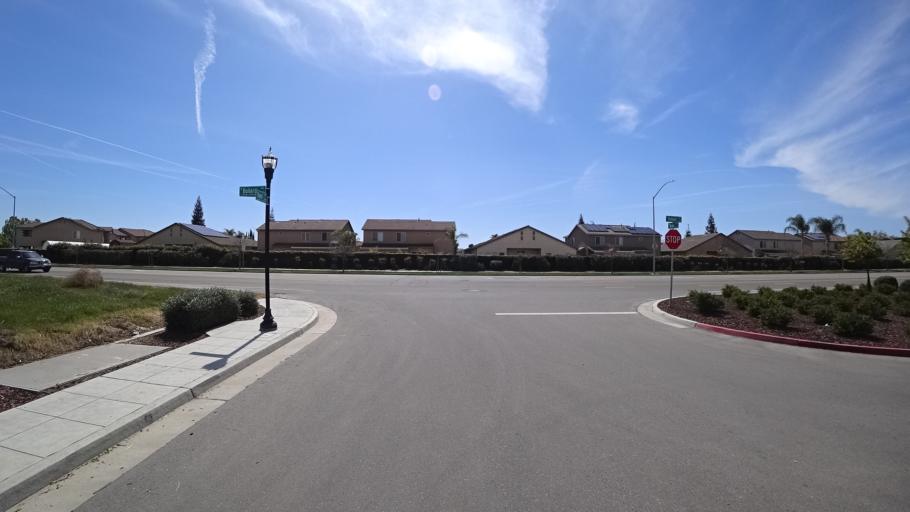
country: US
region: California
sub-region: Fresno County
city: Biola
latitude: 36.8227
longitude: -119.9090
